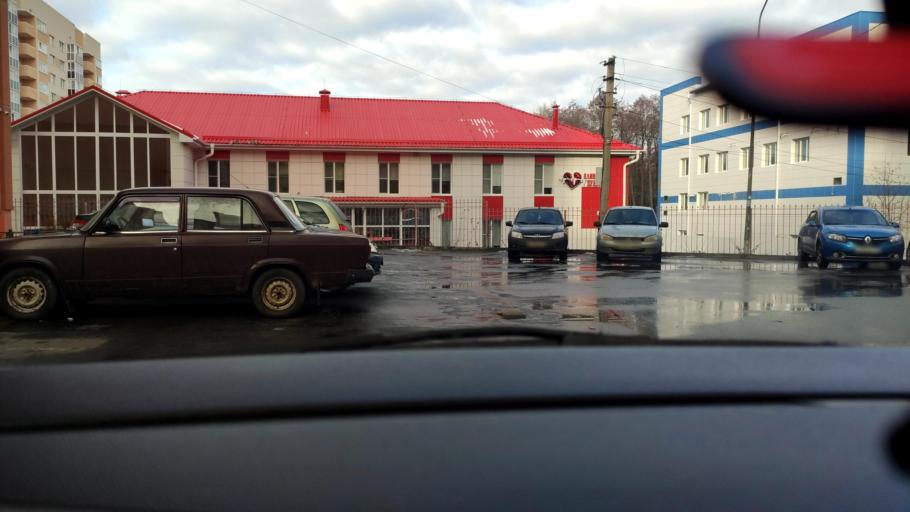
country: RU
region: Voronezj
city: Pridonskoy
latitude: 51.6222
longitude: 39.0632
